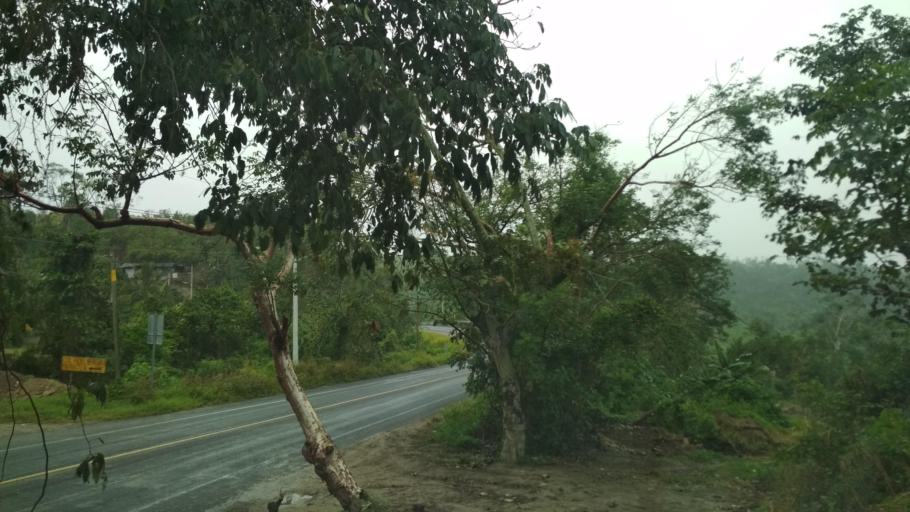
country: MX
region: Veracruz
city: Papantla de Olarte
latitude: 20.4677
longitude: -97.3153
